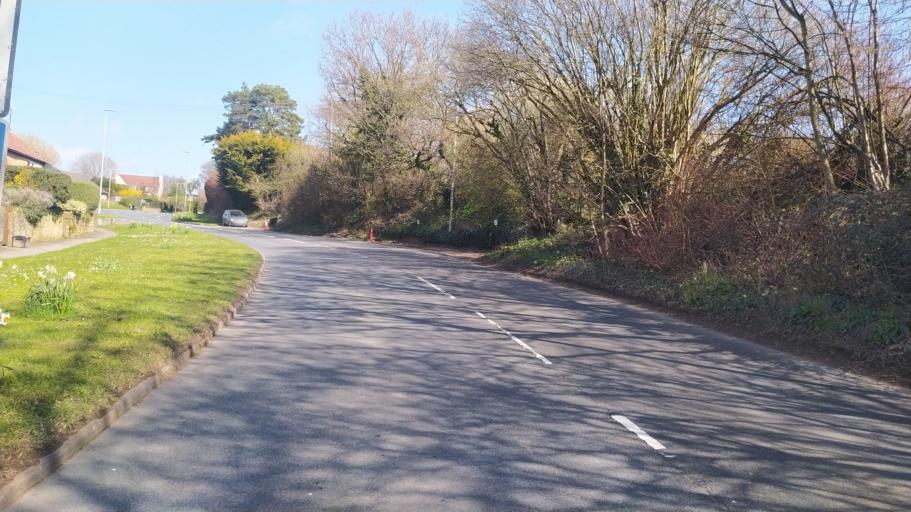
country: GB
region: England
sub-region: Somerset
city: Crewkerne
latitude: 50.8941
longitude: -2.7927
